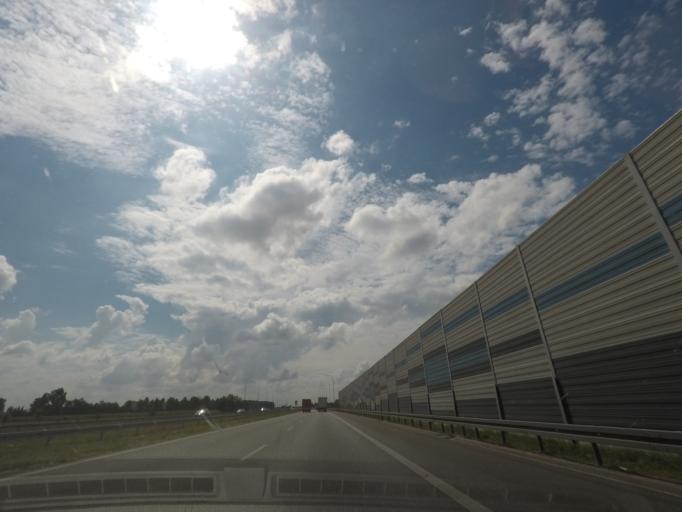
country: PL
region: Lodz Voivodeship
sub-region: Powiat leczycki
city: Piatek
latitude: 52.0140
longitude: 19.5423
